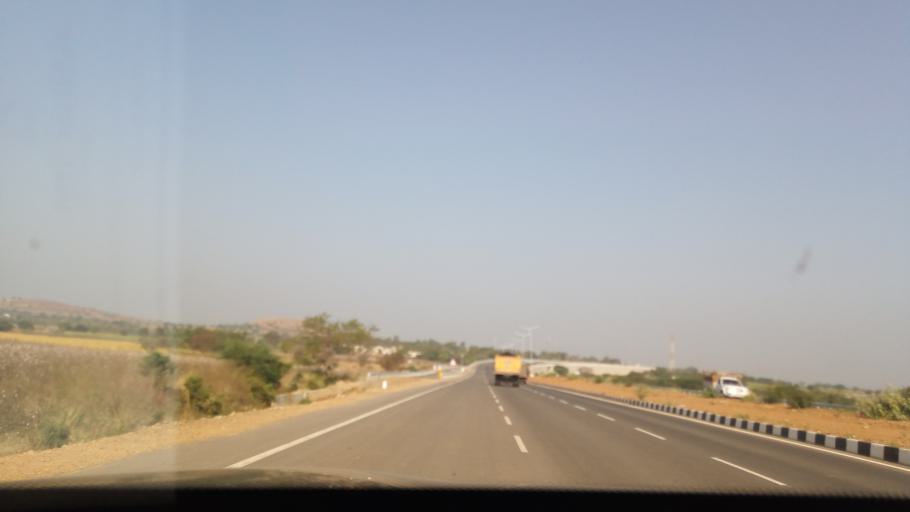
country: IN
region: Karnataka
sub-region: Haveri
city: Haveri
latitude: 14.7539
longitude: 75.4460
